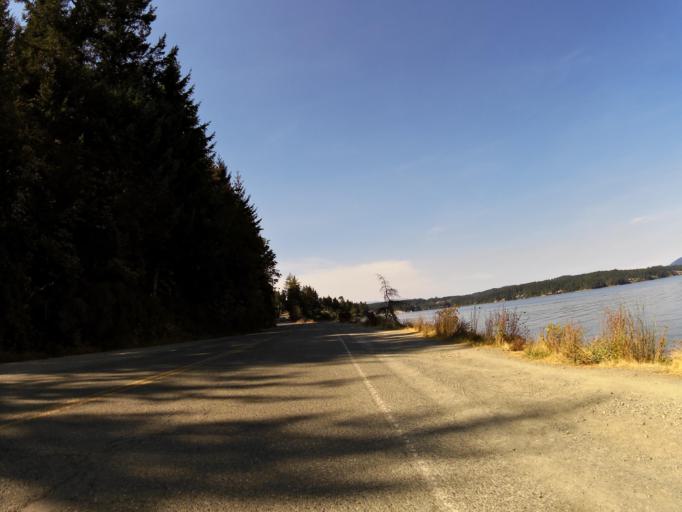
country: CA
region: British Columbia
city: North Saanich
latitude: 48.6344
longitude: -123.5334
